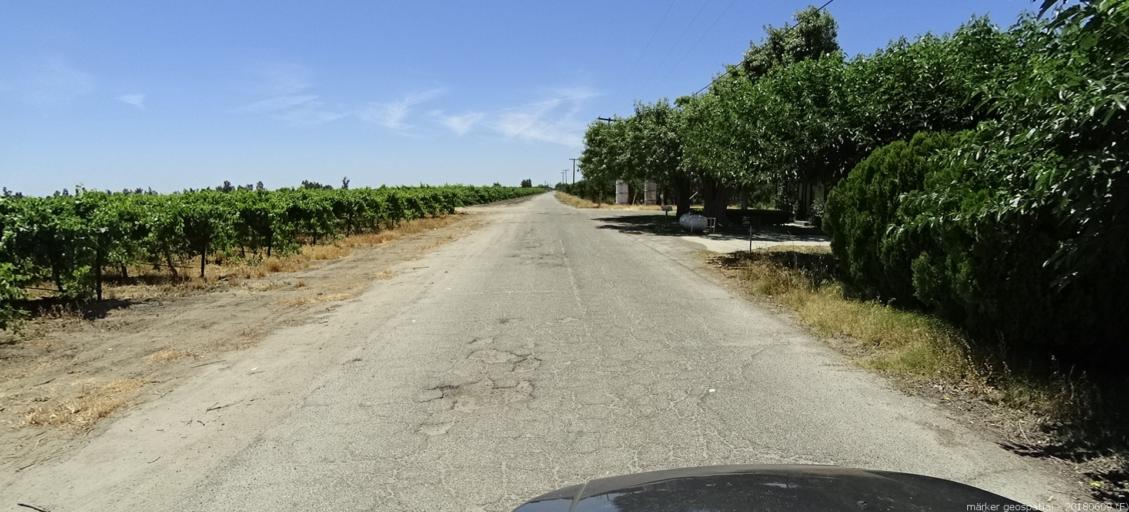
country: US
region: California
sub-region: Madera County
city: Parkwood
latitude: 36.9062
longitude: -120.0742
